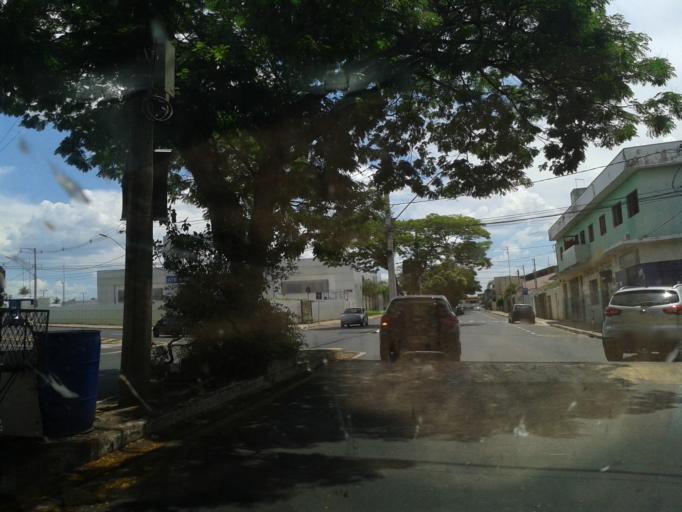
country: BR
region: Minas Gerais
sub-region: Uberaba
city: Uberaba
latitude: -19.7416
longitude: -47.9569
